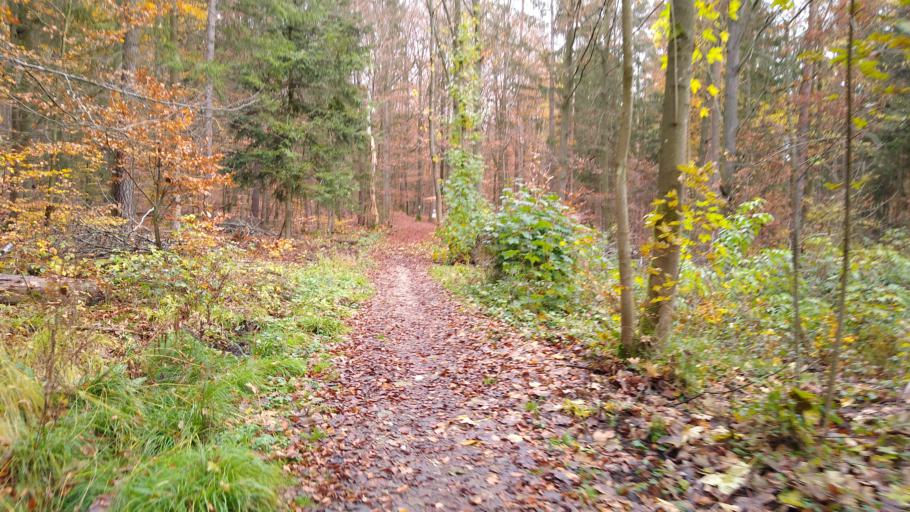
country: DE
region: Bavaria
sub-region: Regierungsbezirk Mittelfranken
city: Kalchreuth
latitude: 49.5470
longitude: 11.1075
